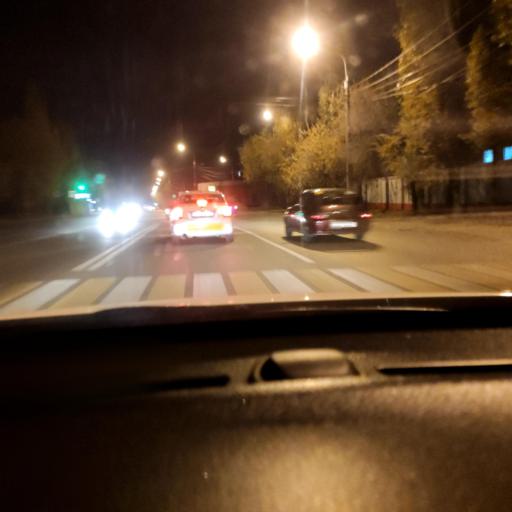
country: RU
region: Voronezj
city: Voronezh
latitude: 51.6383
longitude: 39.2644
